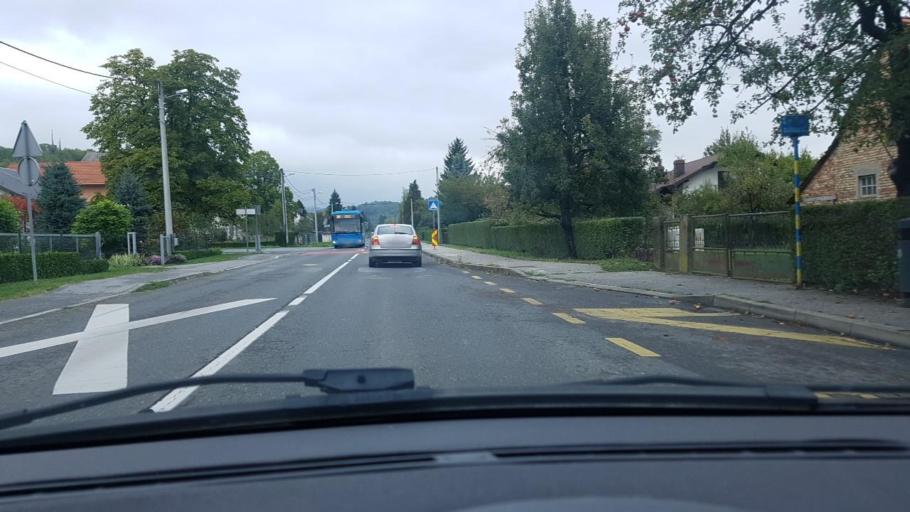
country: HR
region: Grad Zagreb
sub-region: Sesvete
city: Sesvete
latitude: 45.8779
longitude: 16.1153
